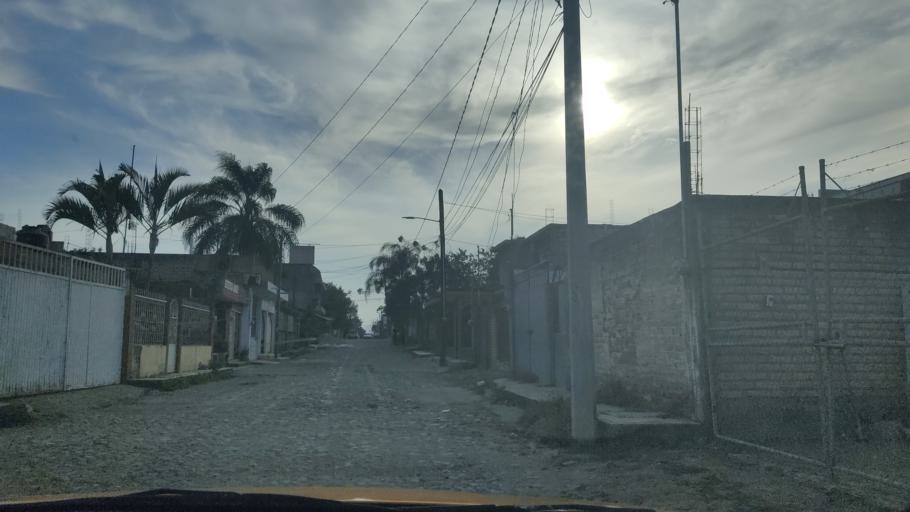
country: MX
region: Nayarit
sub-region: Tepic
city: La Corregidora
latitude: 21.4517
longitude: -104.8199
